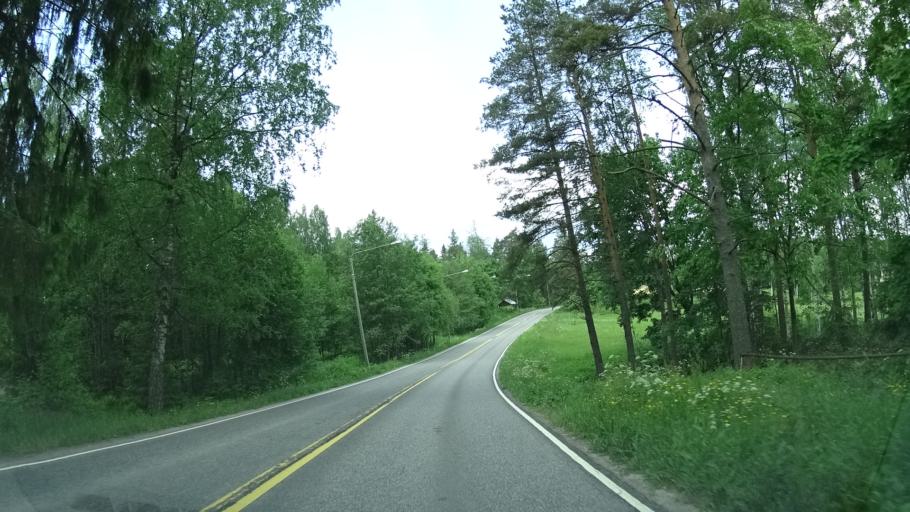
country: FI
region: Uusimaa
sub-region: Helsinki
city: Kirkkonummi
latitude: 60.2081
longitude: 24.4901
